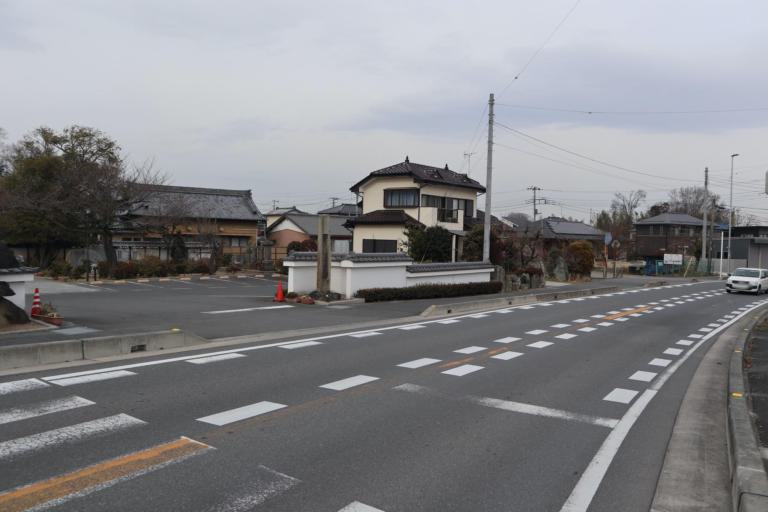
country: JP
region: Saitama
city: Gyoda
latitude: 36.1620
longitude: 139.4834
